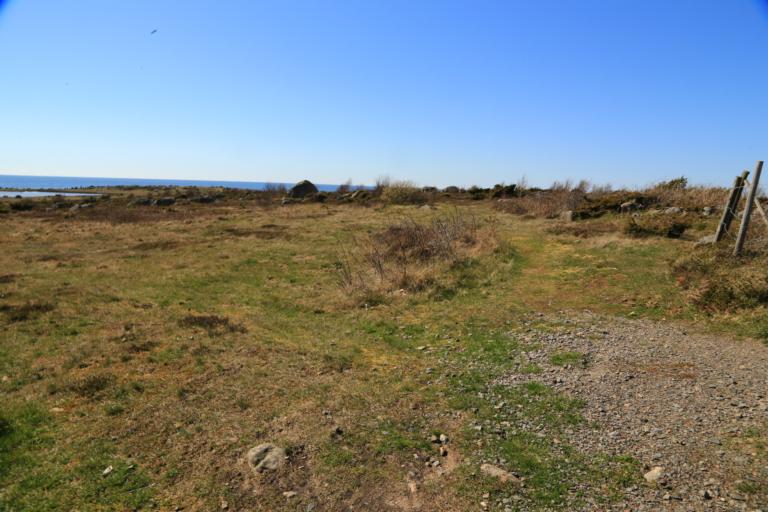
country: SE
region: Halland
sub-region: Varbergs Kommun
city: Traslovslage
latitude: 57.0442
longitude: 12.2900
